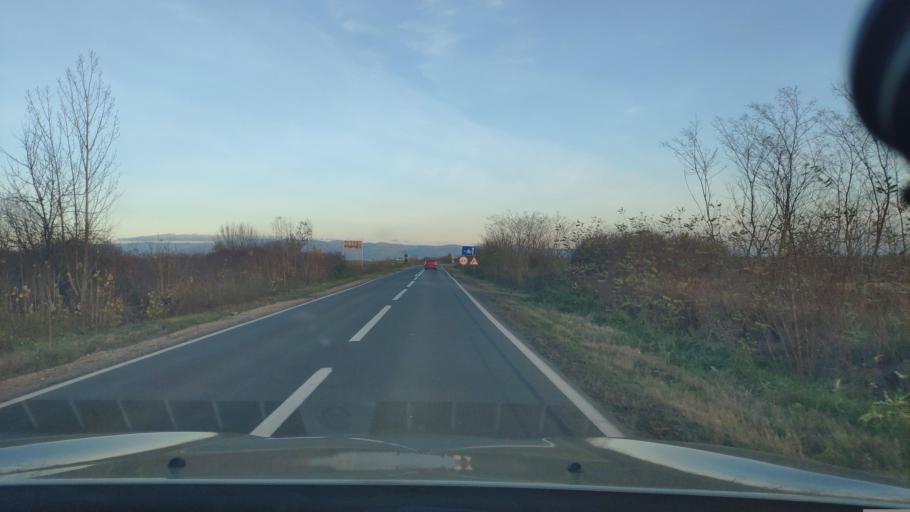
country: RO
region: Satu Mare
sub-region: Comuna Mediesu Aurit
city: Mediesu Aurit
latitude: 47.7717
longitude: 23.1365
